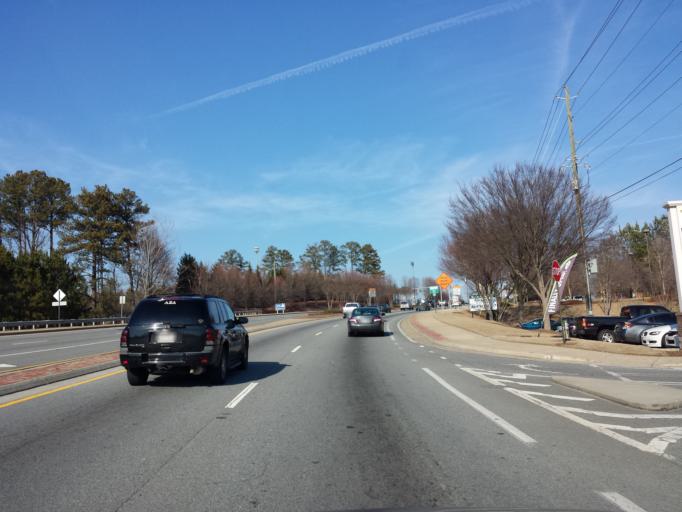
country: US
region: Georgia
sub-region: Cobb County
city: Kennesaw
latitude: 34.0303
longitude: -84.5833
